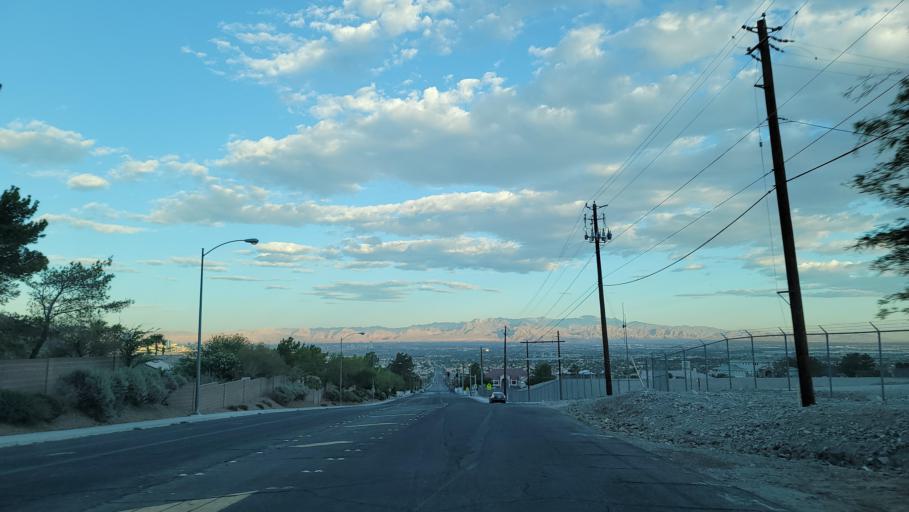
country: US
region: Nevada
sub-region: Clark County
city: Sunrise Manor
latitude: 36.1812
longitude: -115.0182
